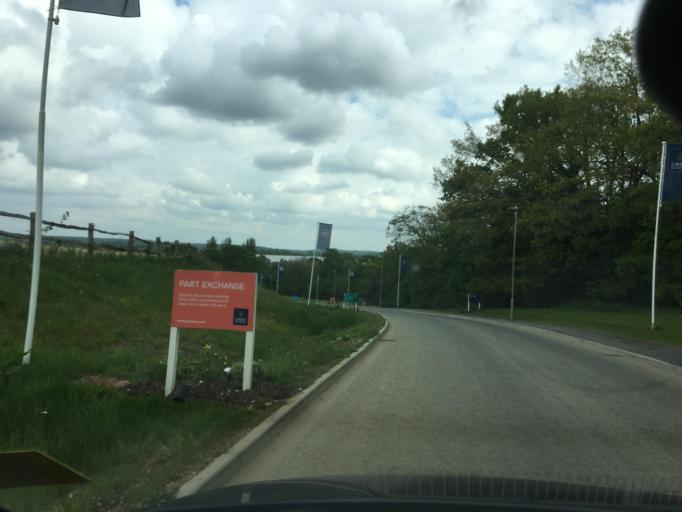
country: GB
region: England
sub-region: Surrey
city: Frimley
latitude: 51.3188
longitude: -0.7711
